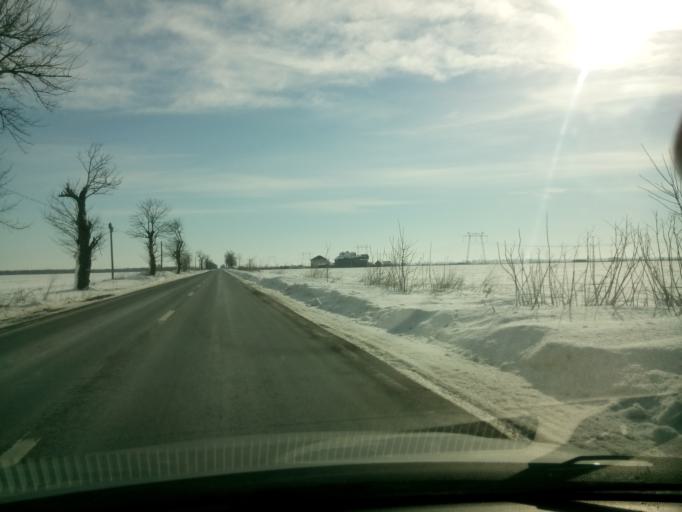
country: RO
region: Calarasi
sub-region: Comuna Frumusani
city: Frumusani
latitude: 44.2654
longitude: 26.3511
